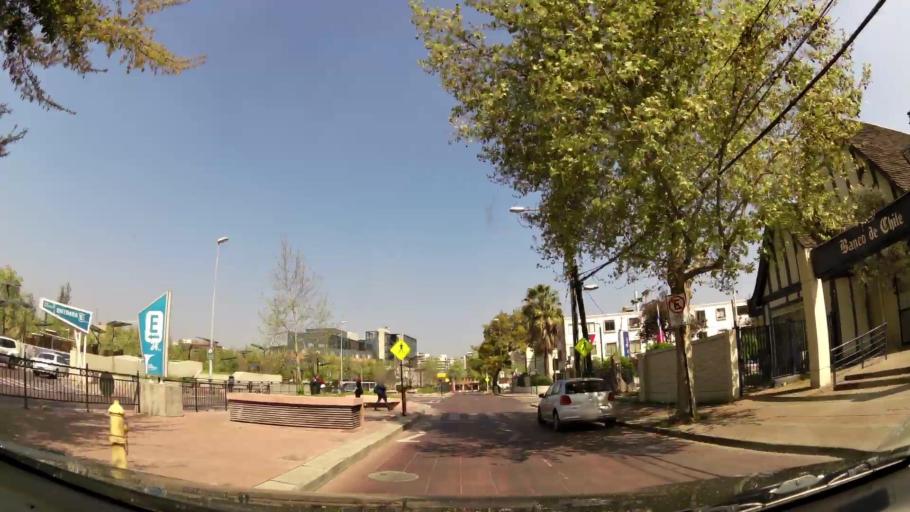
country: CL
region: Santiago Metropolitan
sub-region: Provincia de Santiago
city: Villa Presidente Frei, Nunoa, Santiago, Chile
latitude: -33.3999
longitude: -70.5930
